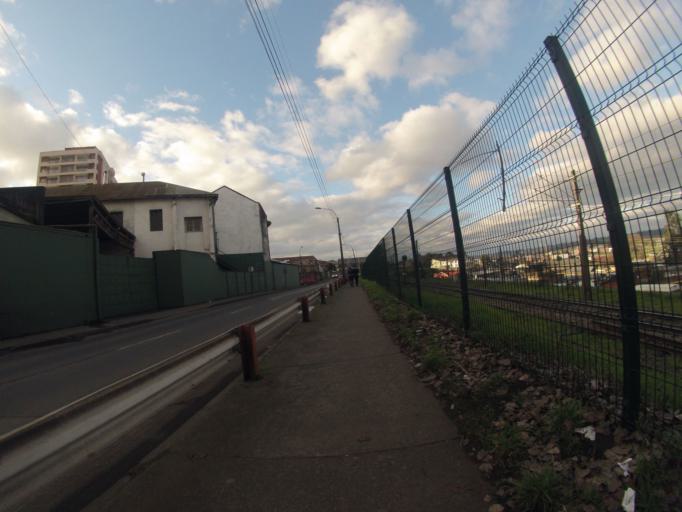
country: CL
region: Araucania
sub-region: Provincia de Cautin
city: Temuco
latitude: -38.7409
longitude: -72.5845
